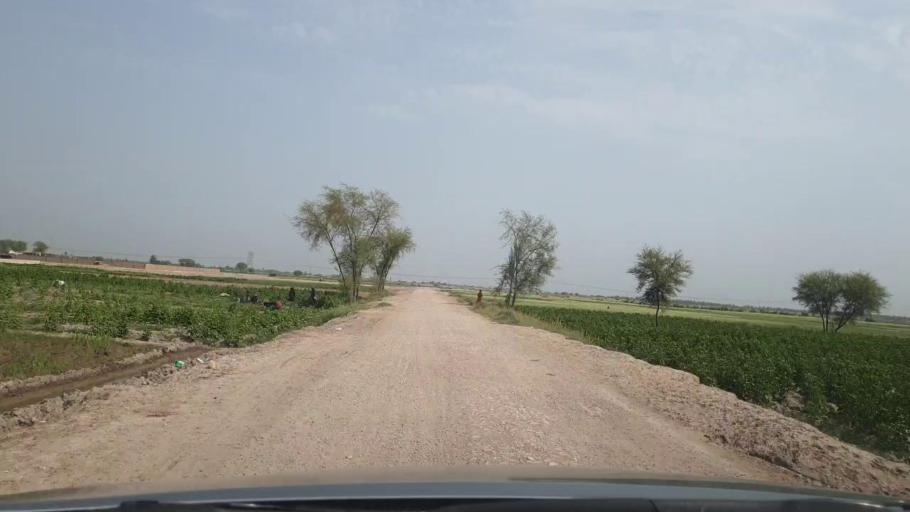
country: PK
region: Sindh
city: Rohri
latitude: 27.6654
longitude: 69.0260
